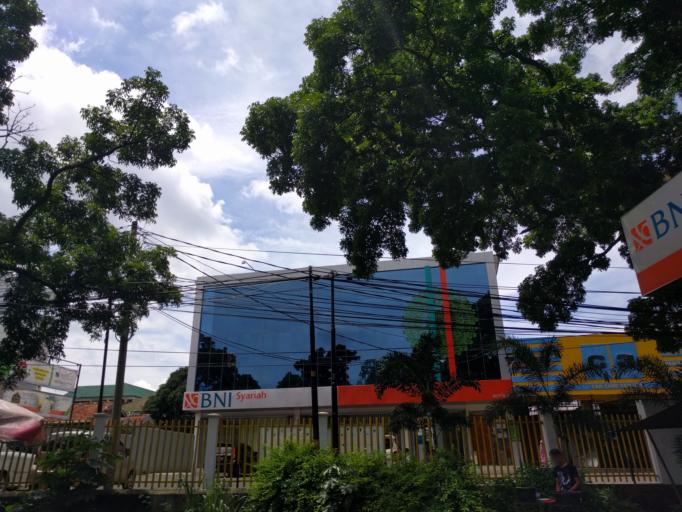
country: ID
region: West Java
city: Bogor
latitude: -6.5754
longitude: 106.8079
